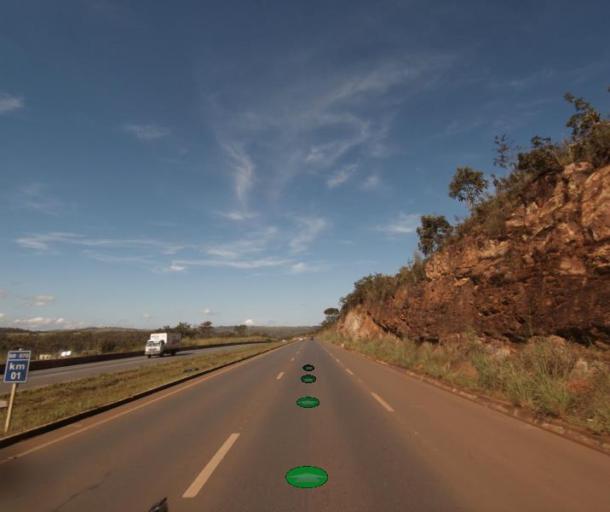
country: BR
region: Federal District
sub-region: Brasilia
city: Brasilia
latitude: -15.7755
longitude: -48.2326
